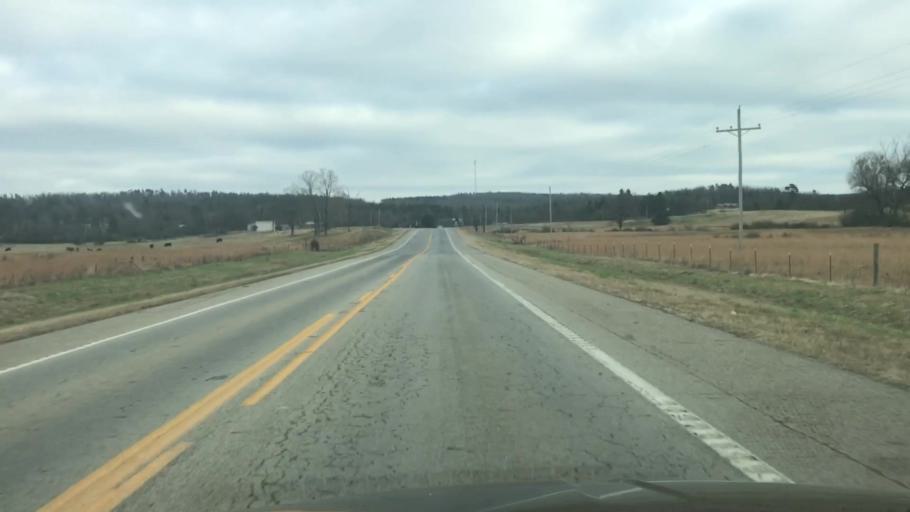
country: US
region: Arkansas
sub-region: Scott County
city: Waldron
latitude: 34.8037
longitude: -94.0408
